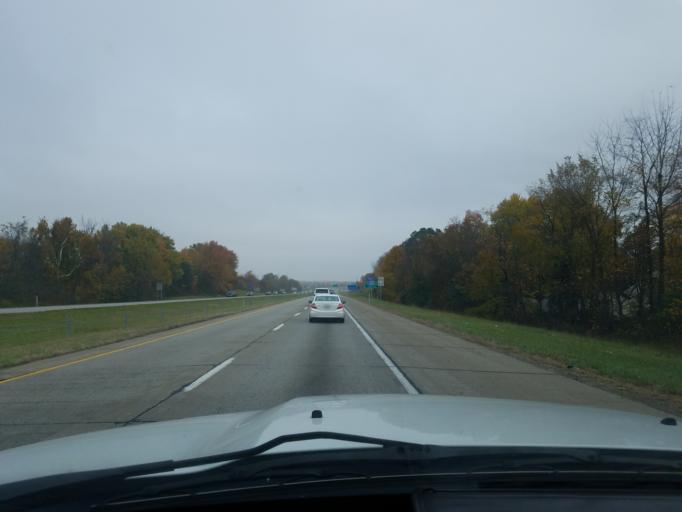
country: US
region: Indiana
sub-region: Floyd County
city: New Albany
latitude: 38.3392
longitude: -85.8114
